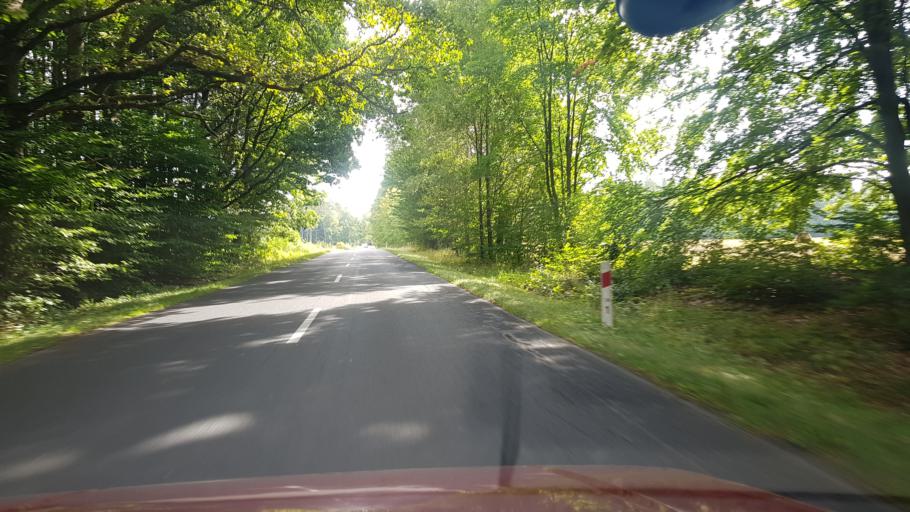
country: PL
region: West Pomeranian Voivodeship
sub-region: Powiat koszalinski
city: Polanow
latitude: 54.1170
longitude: 16.7357
